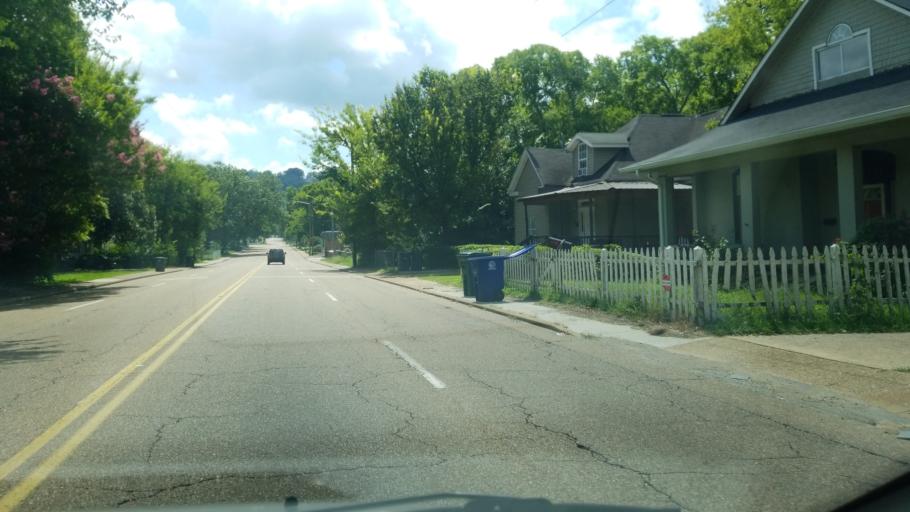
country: US
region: Tennessee
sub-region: Hamilton County
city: East Ridge
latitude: 35.0316
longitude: -85.2713
